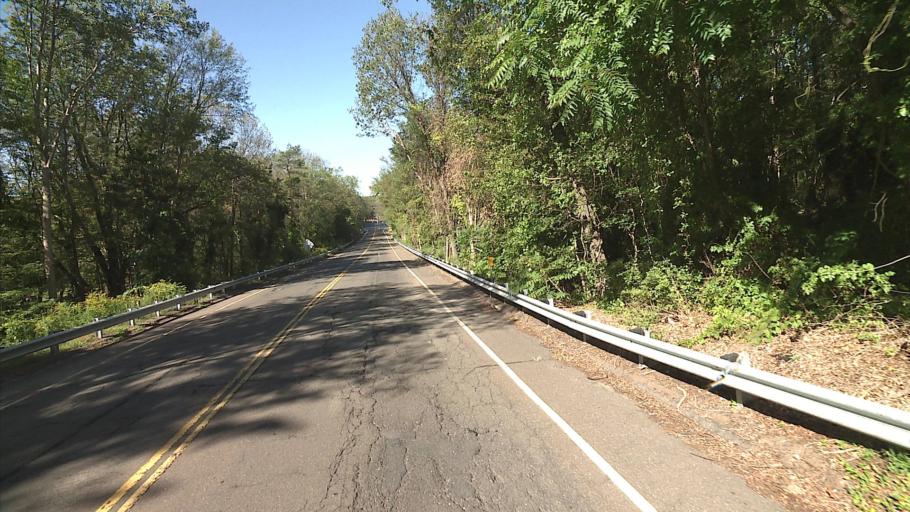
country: US
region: Connecticut
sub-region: Middlesex County
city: Higganum
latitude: 41.5126
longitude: -72.5887
